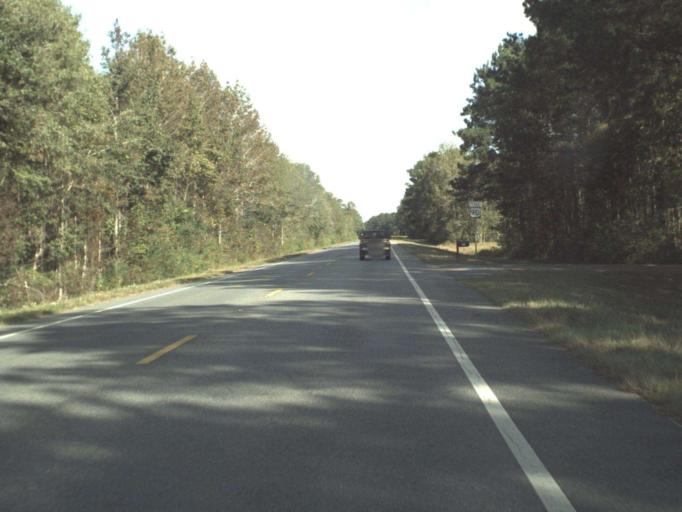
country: US
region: Florida
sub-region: Holmes County
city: Bonifay
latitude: 30.7782
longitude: -85.6113
